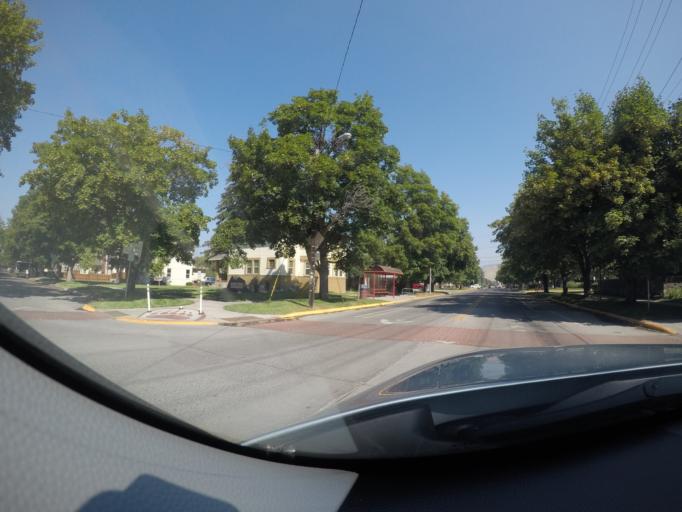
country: US
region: Montana
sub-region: Missoula County
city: Missoula
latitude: 46.8601
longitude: -113.9893
